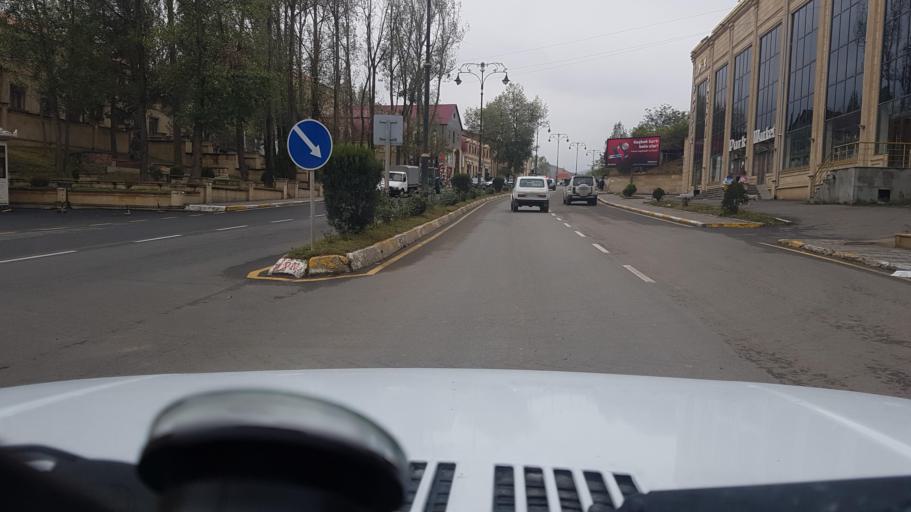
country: AZ
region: Gadabay Rayon
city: Kyadabek
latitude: 40.5777
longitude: 45.8087
